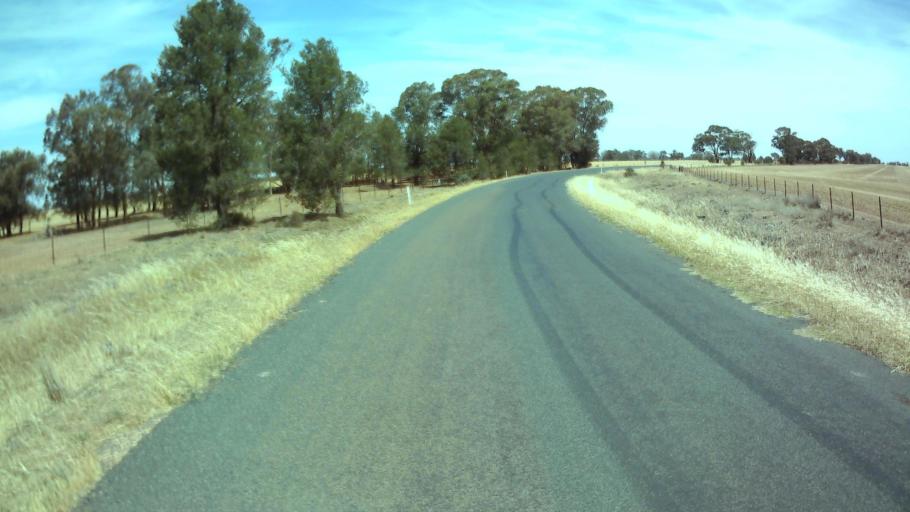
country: AU
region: New South Wales
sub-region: Weddin
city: Grenfell
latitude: -33.9597
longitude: 147.7815
